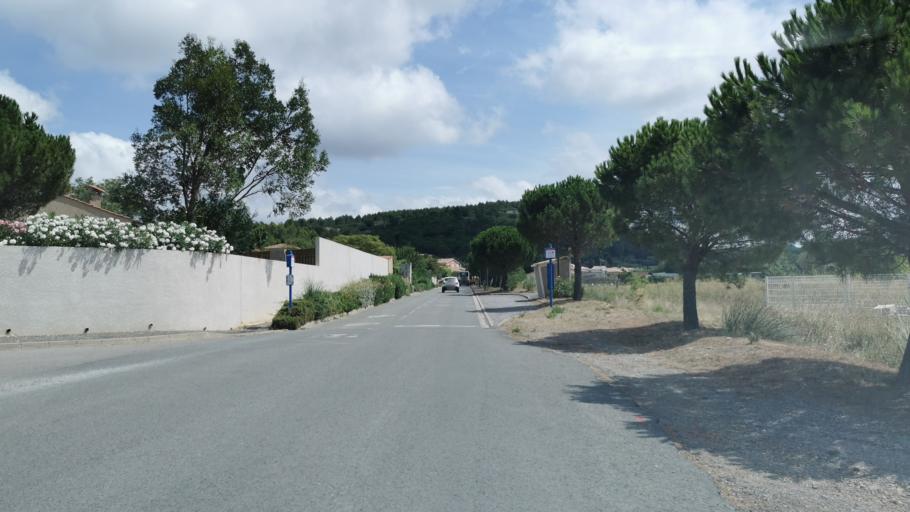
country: FR
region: Languedoc-Roussillon
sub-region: Departement de l'Aude
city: Bizanet
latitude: 43.1664
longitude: 2.8782
